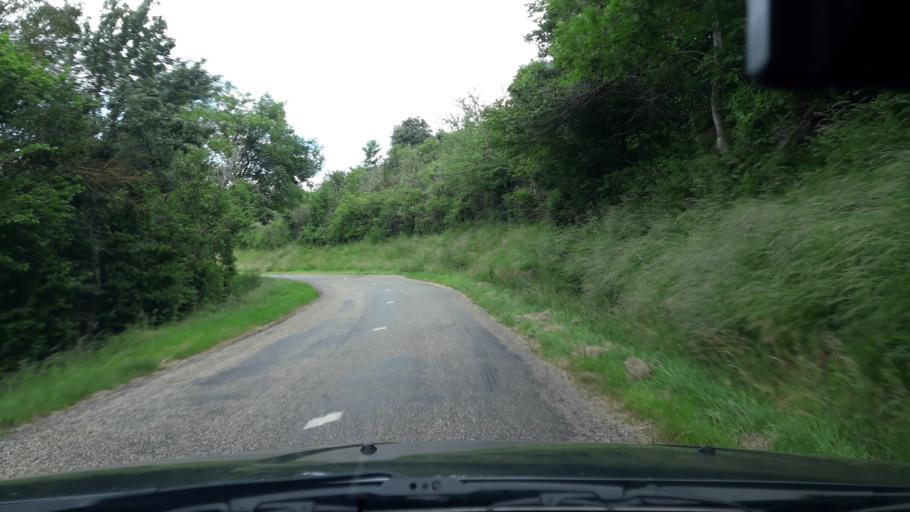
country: FR
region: Rhone-Alpes
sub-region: Departement de l'Ardeche
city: Saint-Priest
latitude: 44.6727
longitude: 4.5335
